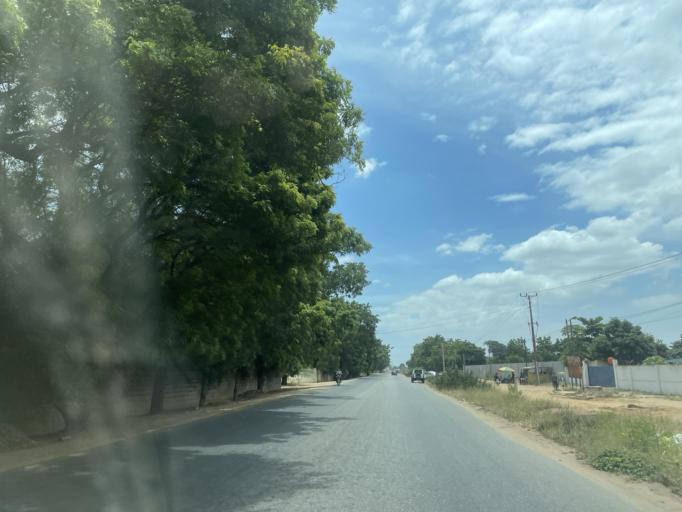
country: AO
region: Luanda
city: Luanda
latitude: -8.9235
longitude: 13.3989
